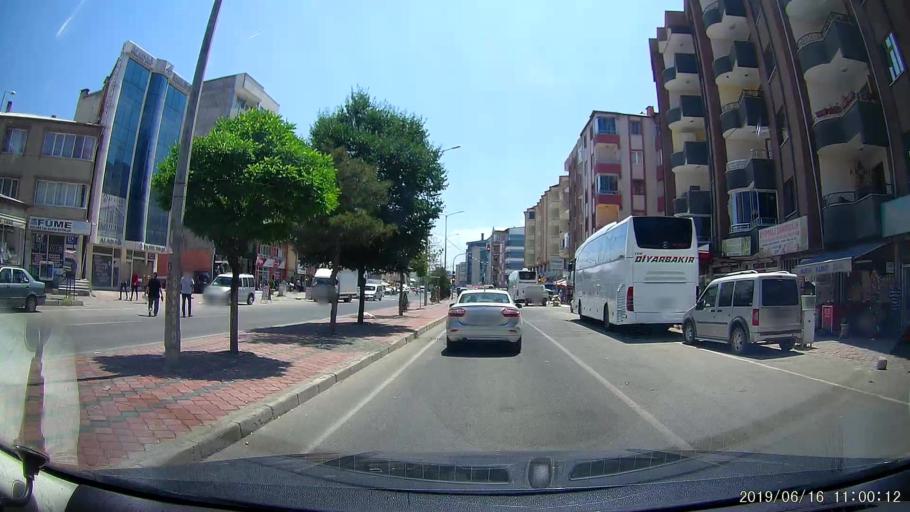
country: TR
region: Igdir
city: Igdir
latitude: 39.9190
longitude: 44.0422
